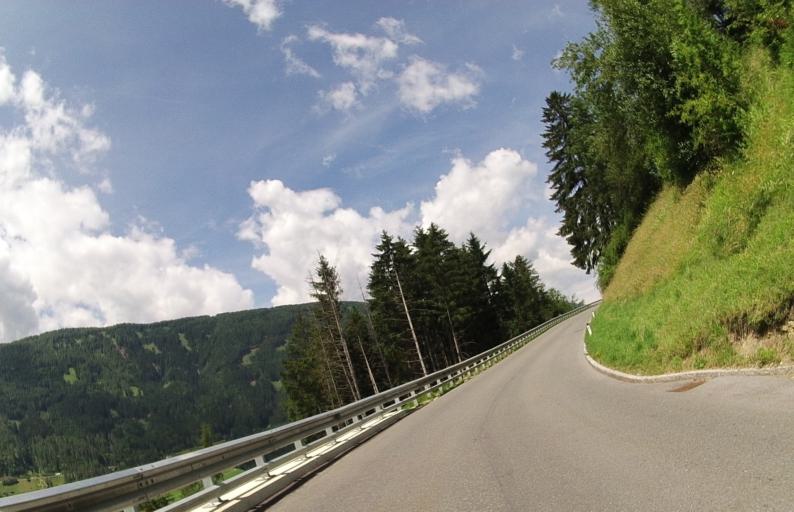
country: AT
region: Tyrol
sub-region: Politischer Bezirk Innsbruck Land
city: Ellbogen
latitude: 47.1638
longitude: 11.4524
